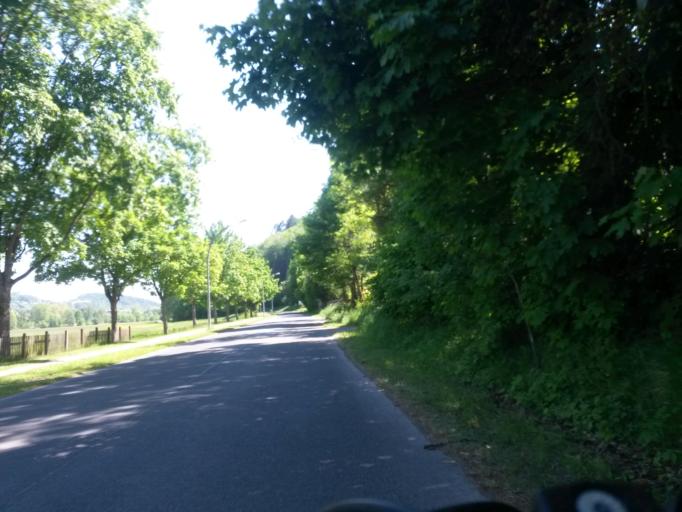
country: DE
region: Bavaria
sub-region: Regierungsbezirk Unterfranken
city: Bad Kissingen
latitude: 50.2081
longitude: 10.0675
